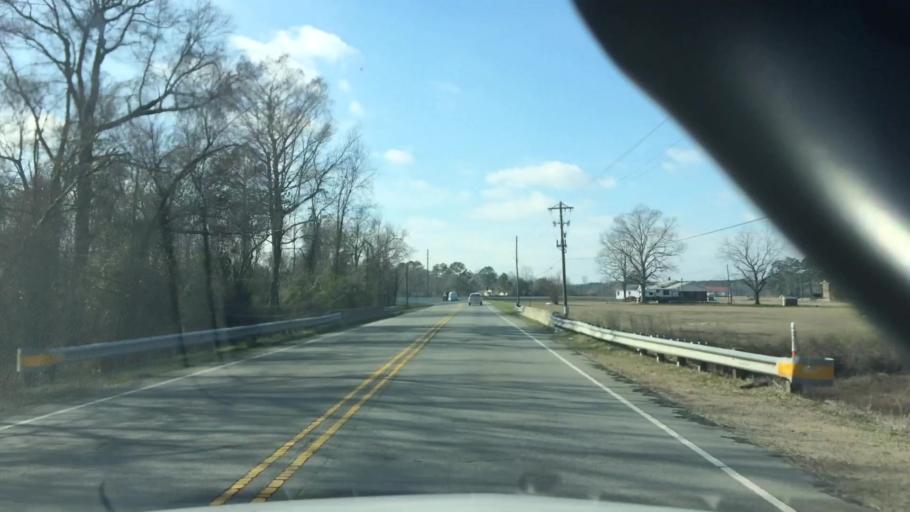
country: US
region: North Carolina
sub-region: Duplin County
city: Wallace
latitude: 34.7850
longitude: -77.9044
